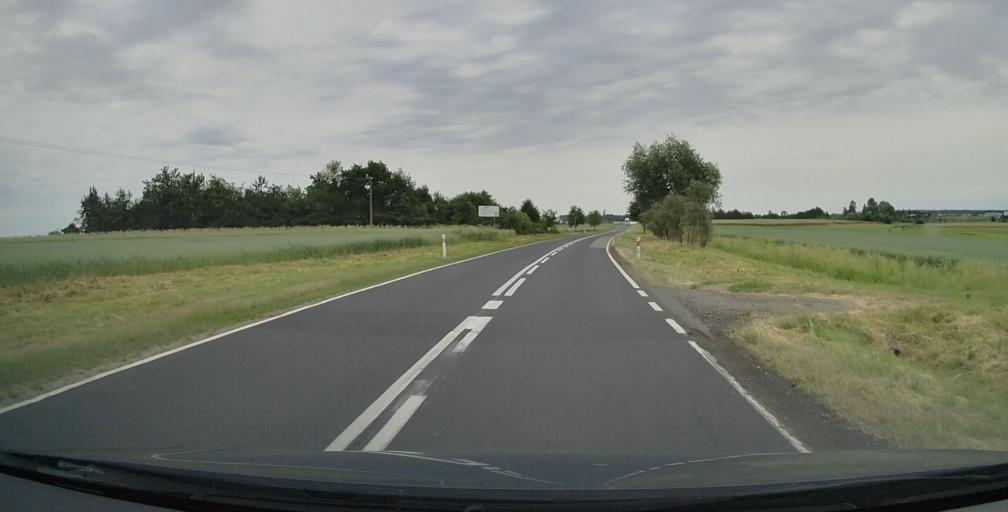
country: PL
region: Lublin Voivodeship
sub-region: Powiat bialski
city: Konstantynow
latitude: 52.2186
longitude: 23.0655
